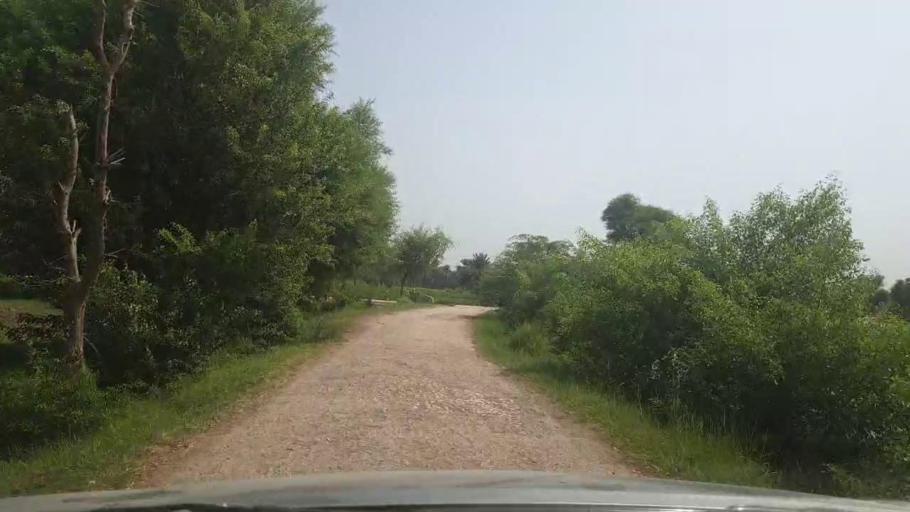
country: PK
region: Sindh
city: Pano Aqil
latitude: 27.8784
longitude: 69.1146
